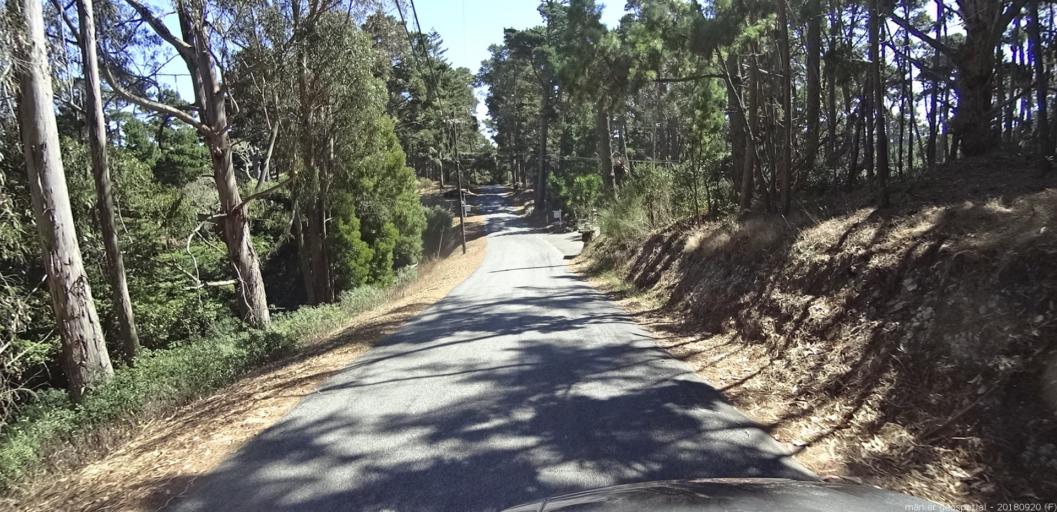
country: US
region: California
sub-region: Monterey County
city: Carmel-by-the-Sea
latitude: 36.5676
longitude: -121.8931
